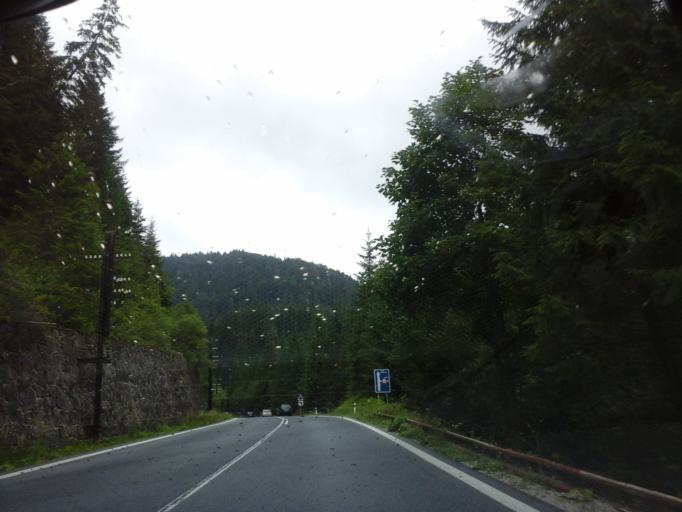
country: SK
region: Kosicky
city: Dobsina
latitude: 48.8843
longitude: 20.3173
